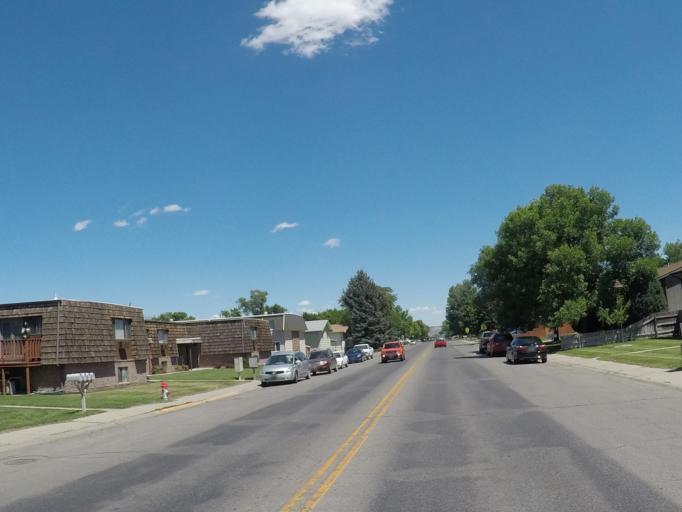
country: US
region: Montana
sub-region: Yellowstone County
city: Billings
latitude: 45.7625
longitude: -108.5743
